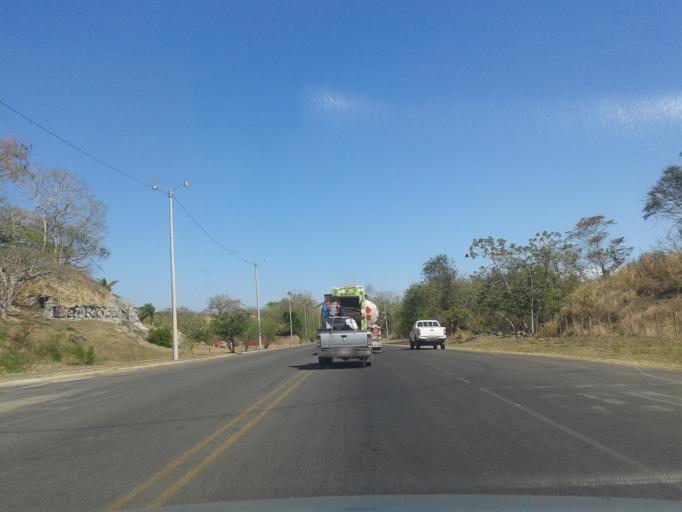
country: CR
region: Puntarenas
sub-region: Canton Central de Puntarenas
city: Chacarita
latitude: 9.9457
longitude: -84.7275
